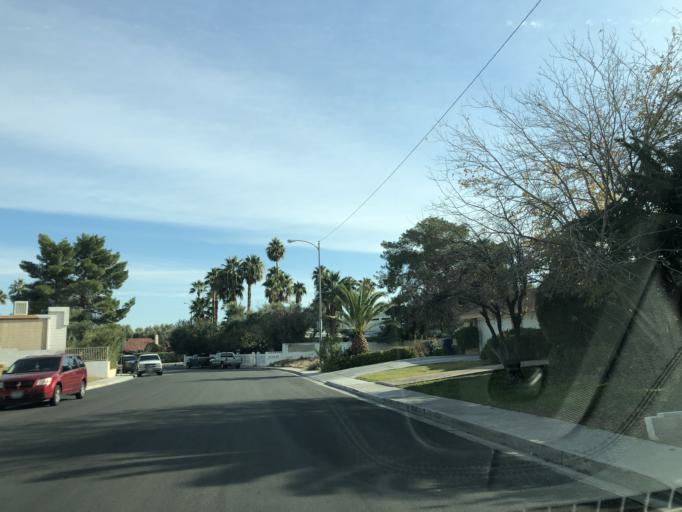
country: US
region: Nevada
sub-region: Clark County
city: Winchester
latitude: 36.1253
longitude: -115.1199
